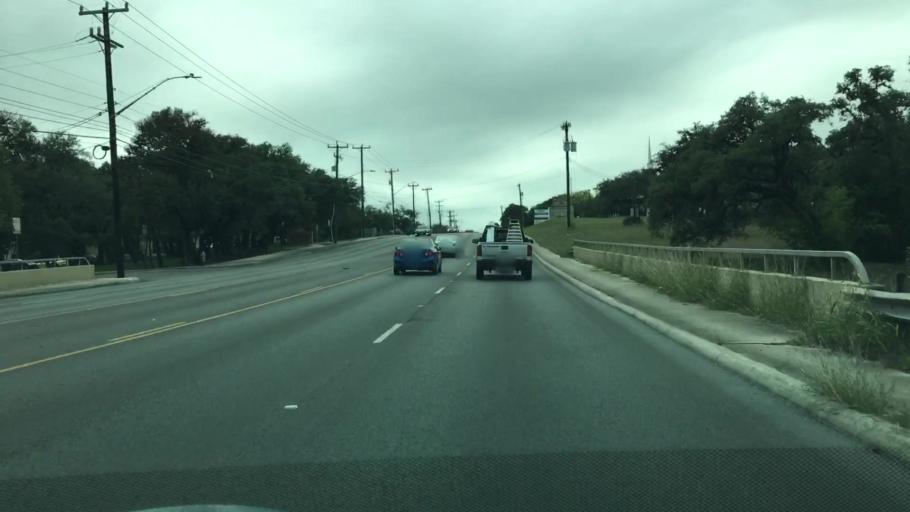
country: US
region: Texas
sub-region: Bexar County
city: Hollywood Park
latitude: 29.5610
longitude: -98.4596
